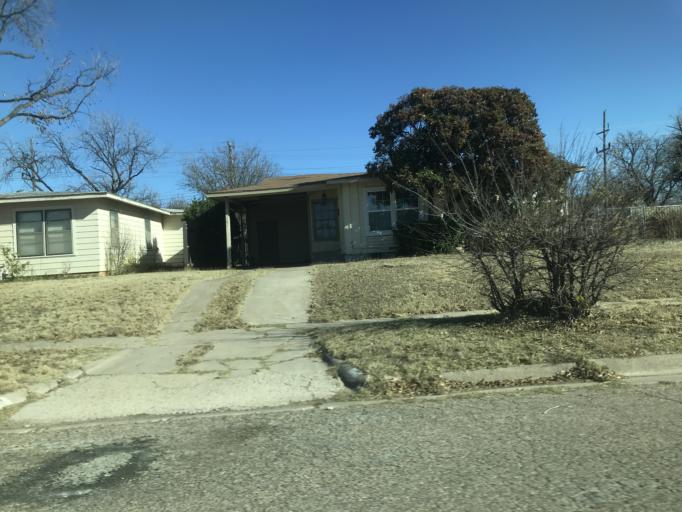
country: US
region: Texas
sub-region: Taylor County
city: Abilene
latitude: 32.4343
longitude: -99.7537
